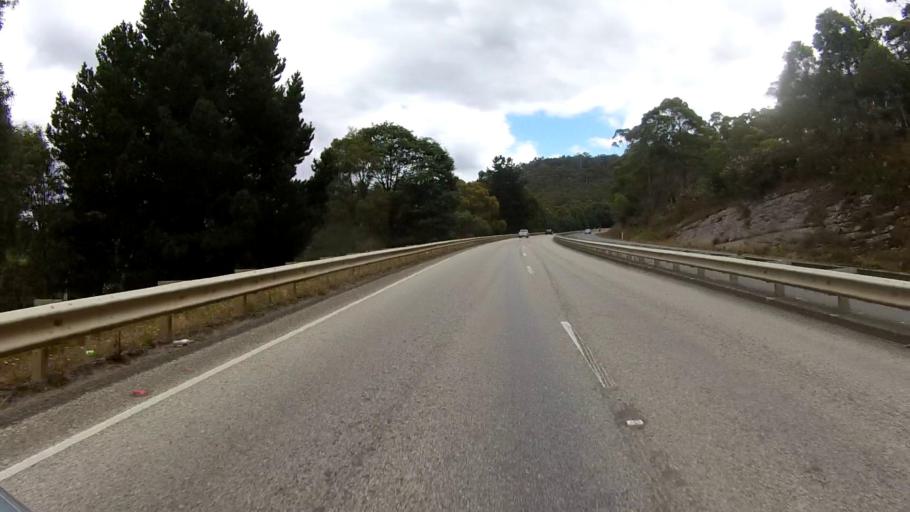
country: AU
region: Tasmania
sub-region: Kingborough
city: Margate
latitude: -42.9858
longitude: 147.1884
